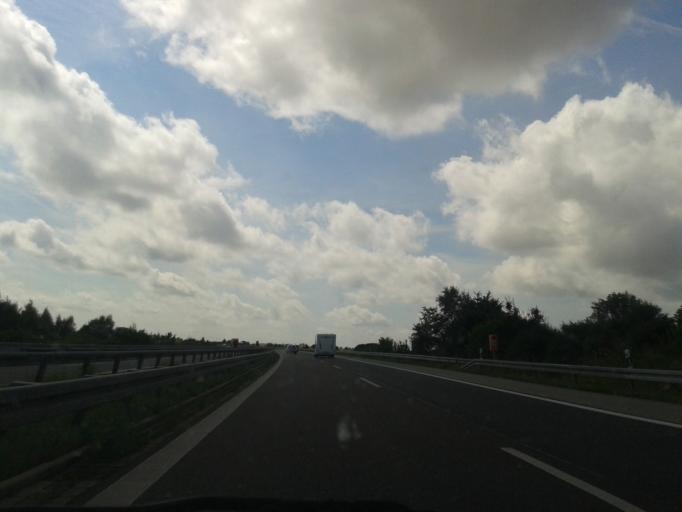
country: DE
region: Brandenburg
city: Grunow
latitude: 53.2940
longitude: 13.9855
